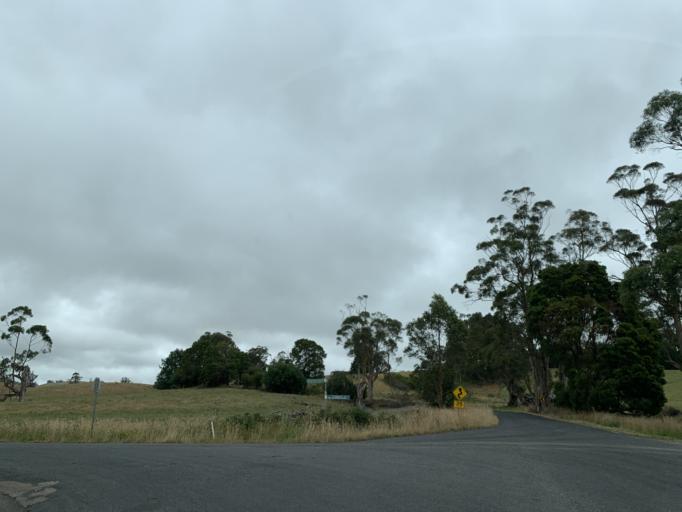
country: AU
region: Victoria
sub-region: Baw Baw
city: Warragul
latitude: -38.2929
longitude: 145.8320
